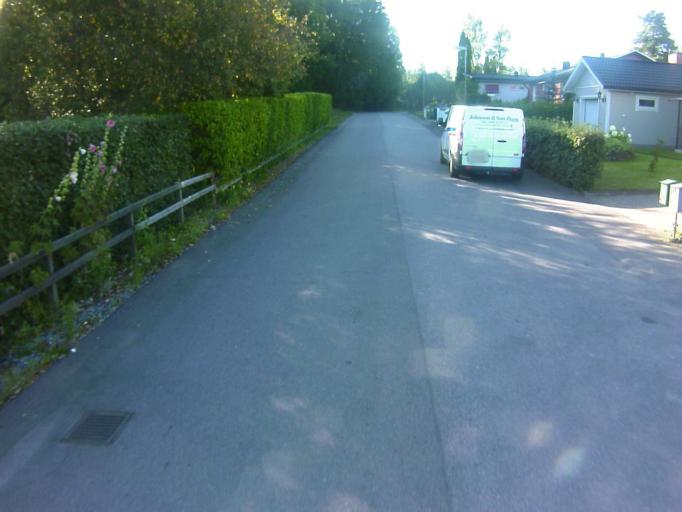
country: SE
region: Soedermanland
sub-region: Eskilstuna Kommun
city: Skogstorp
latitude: 59.3345
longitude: 16.4383
